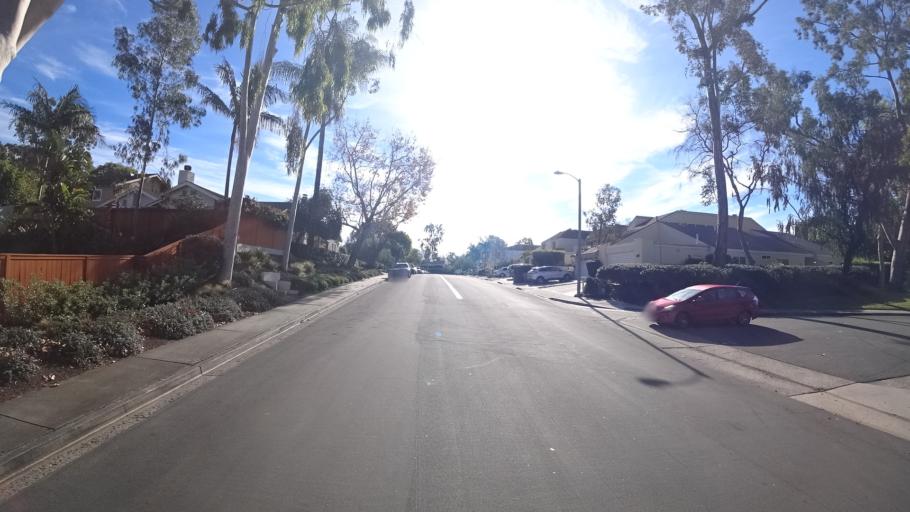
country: US
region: California
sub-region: Orange County
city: Lake Forest
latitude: 33.6375
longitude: -117.7066
